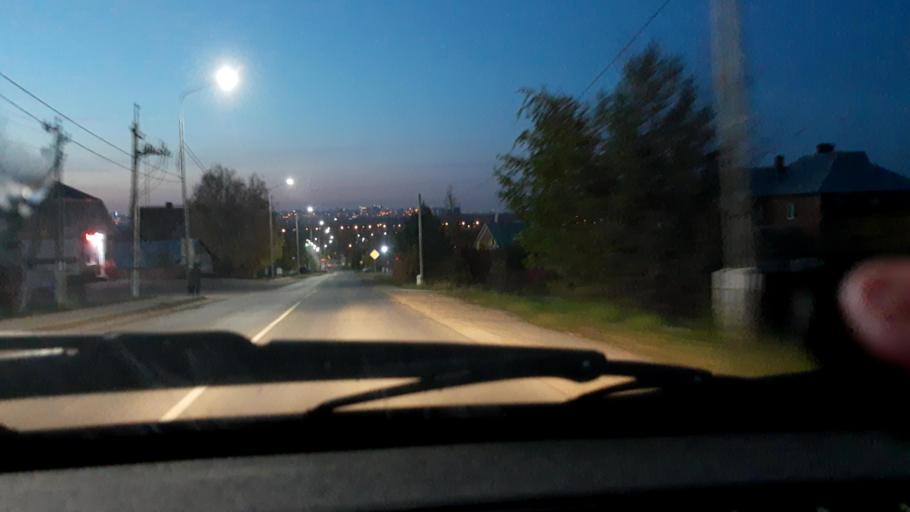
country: RU
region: Bashkortostan
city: Mikhaylovka
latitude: 54.8103
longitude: 55.8875
